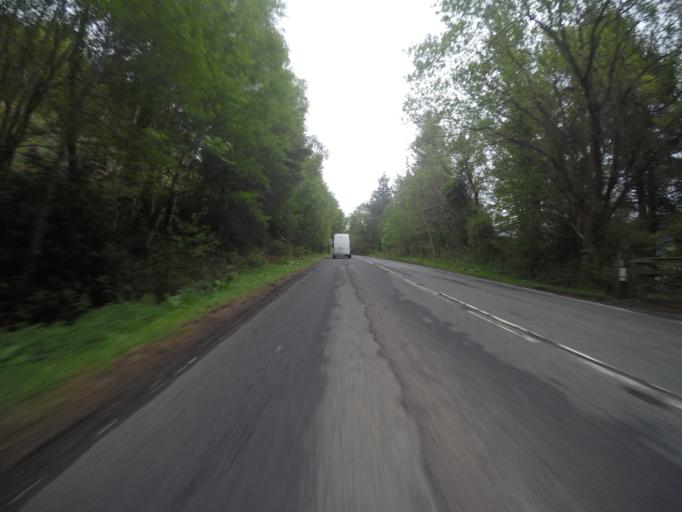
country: GB
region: Scotland
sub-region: Highland
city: Fort William
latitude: 57.2493
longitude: -5.4706
